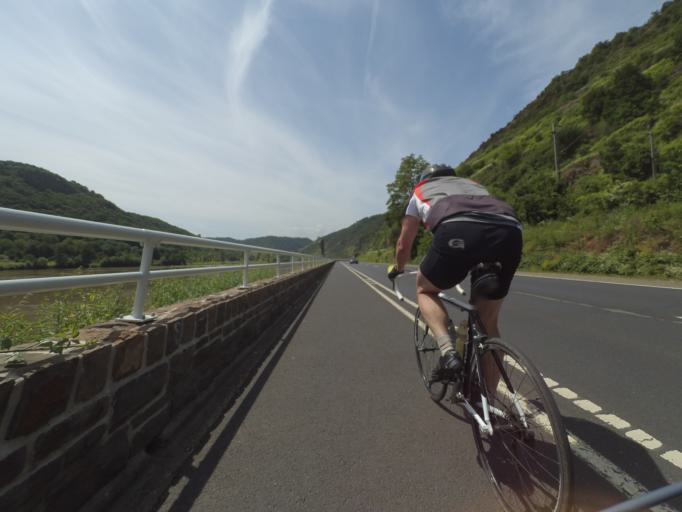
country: DE
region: Rheinland-Pfalz
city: Treis-Karden
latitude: 50.1859
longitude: 7.3257
